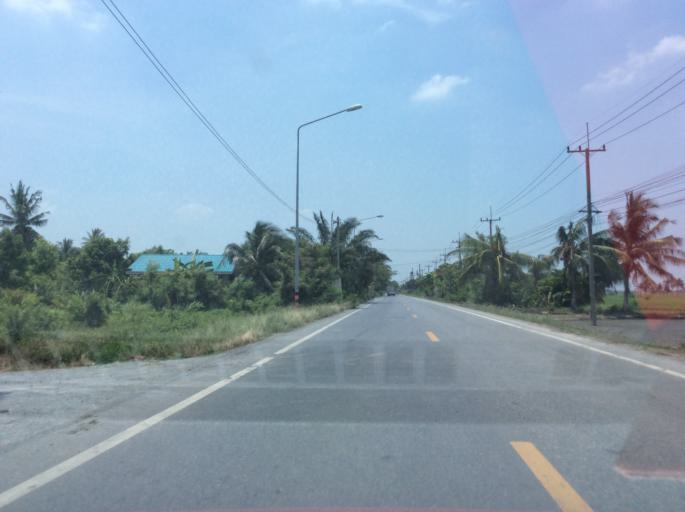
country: TH
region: Pathum Thani
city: Ban Lam Luk Ka
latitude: 13.9995
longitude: 100.7786
